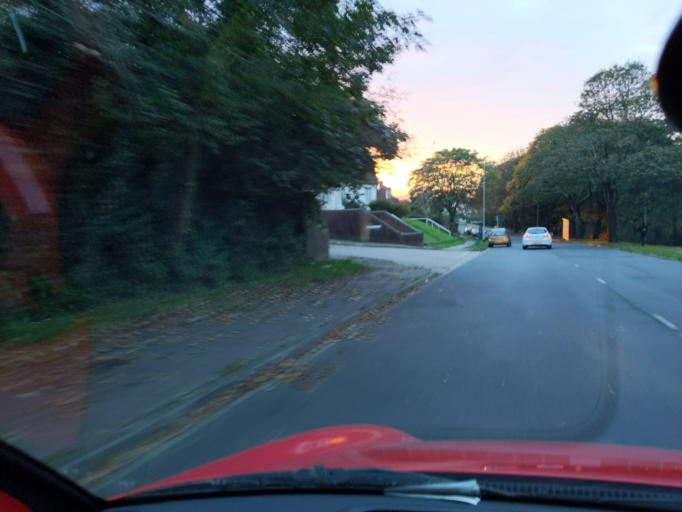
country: GB
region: England
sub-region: Plymouth
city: Plymouth
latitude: 50.3982
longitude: -4.1553
